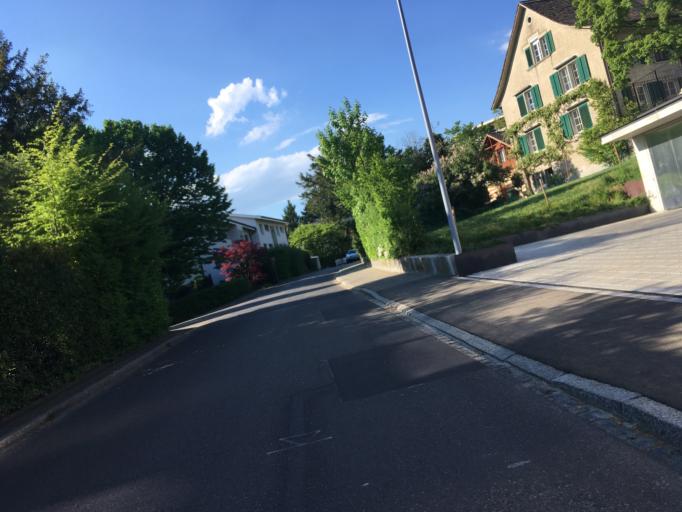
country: CH
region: Zurich
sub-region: Bezirk Meilen
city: Kuesnacht / Heslibach
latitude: 47.3102
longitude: 8.5899
